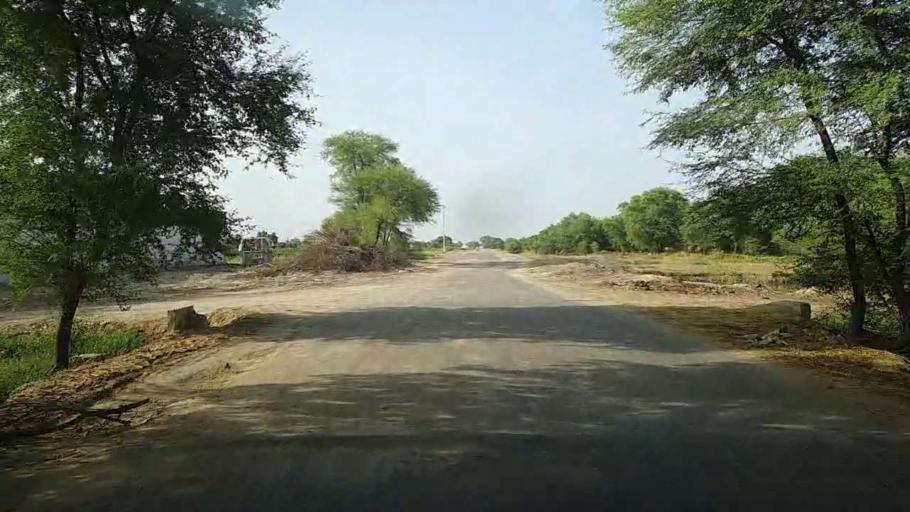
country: PK
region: Sindh
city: Ubauro
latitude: 28.0920
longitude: 69.8446
